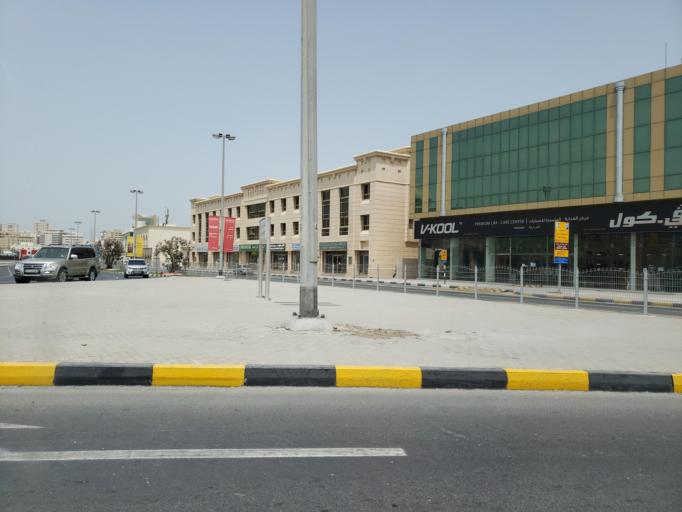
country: AE
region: Ash Shariqah
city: Sharjah
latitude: 25.3569
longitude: 55.4033
